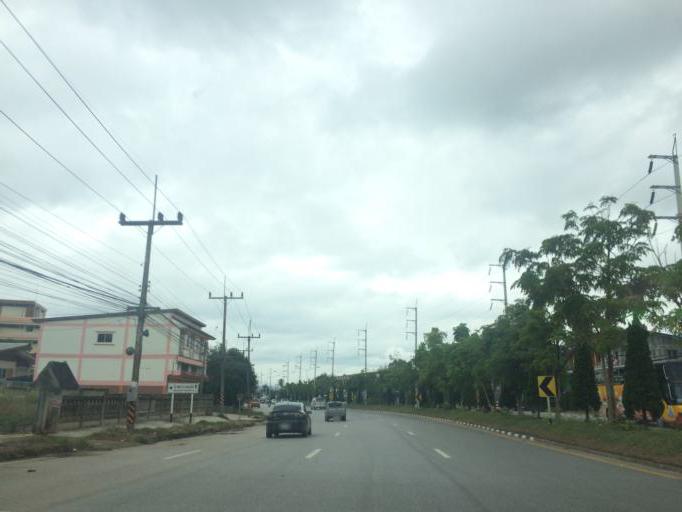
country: TH
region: Chiang Rai
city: Mae Chan
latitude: 20.1335
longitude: 99.8614
